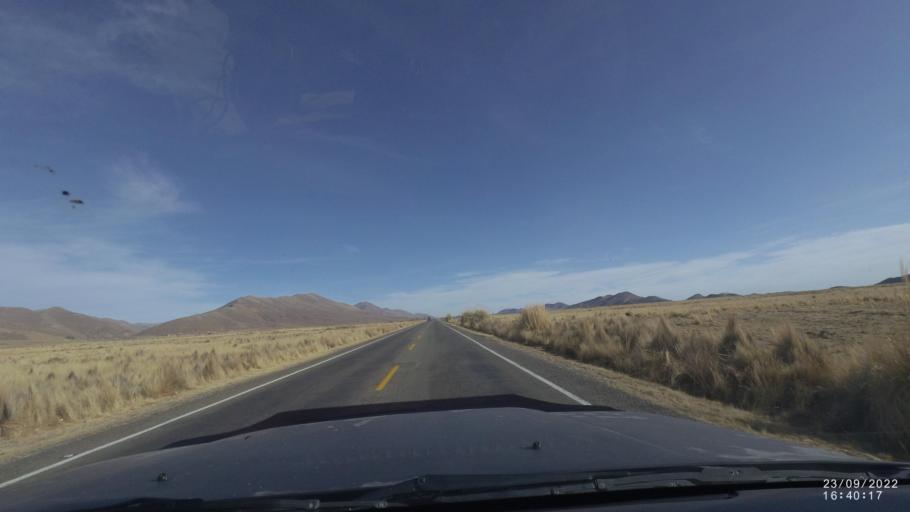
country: BO
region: Oruro
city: Machacamarca
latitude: -18.2737
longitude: -66.9967
